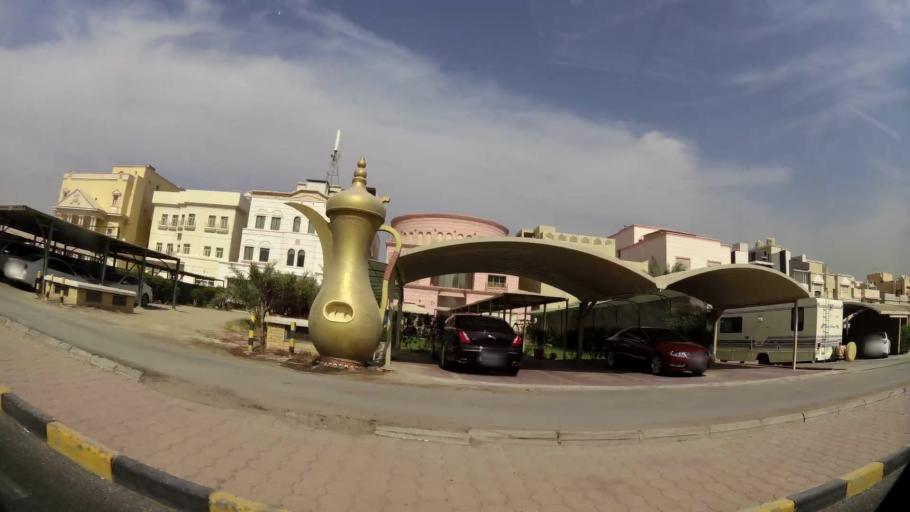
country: KW
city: Bayan
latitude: 29.2773
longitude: 48.0224
